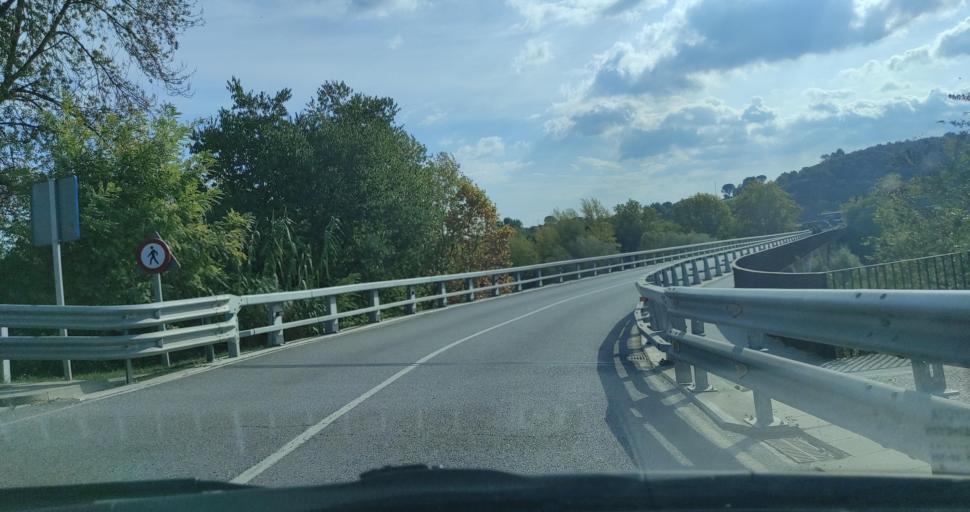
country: ES
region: Catalonia
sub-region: Provincia de Girona
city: Besalu
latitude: 42.2005
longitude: 2.7015
